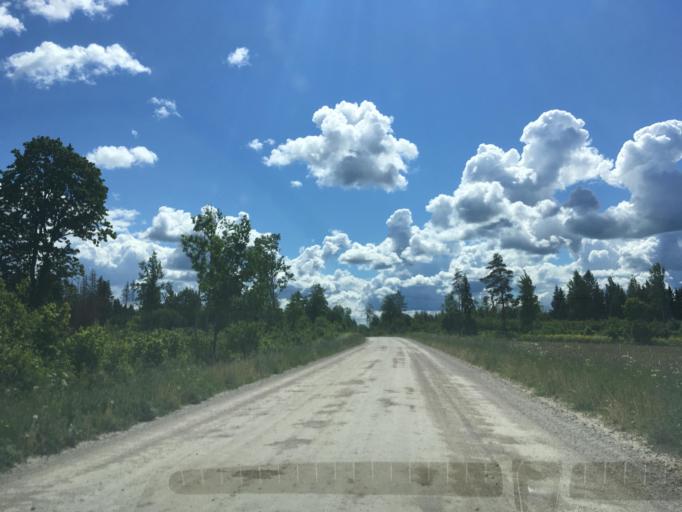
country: EE
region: Harju
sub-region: Nissi vald
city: Turba
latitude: 58.9331
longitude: 24.1510
